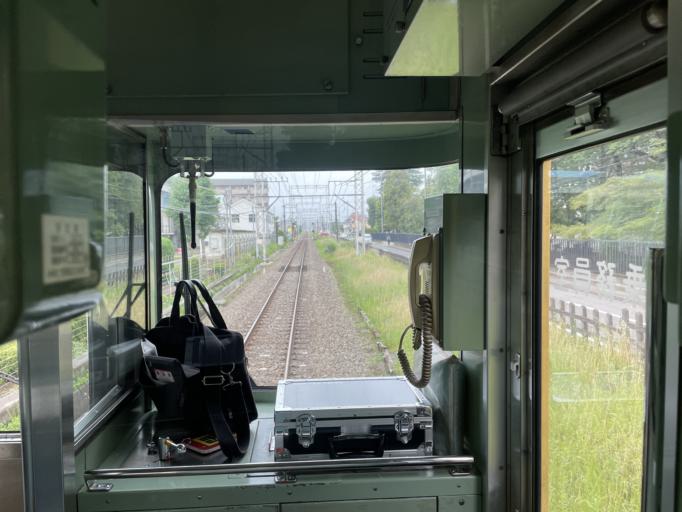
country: JP
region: Tokyo
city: Hino
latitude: 35.7308
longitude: 139.4086
